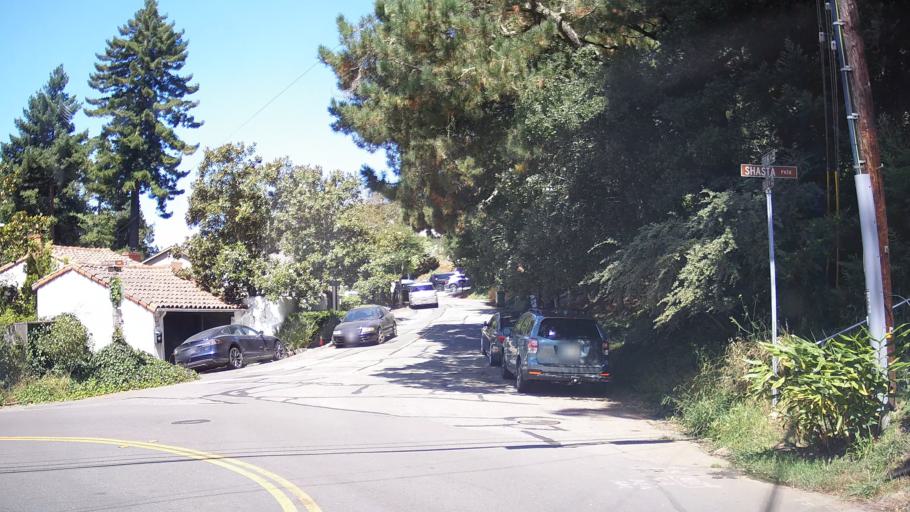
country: US
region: California
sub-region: Alameda County
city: Berkeley
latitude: 37.8891
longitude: -122.2540
